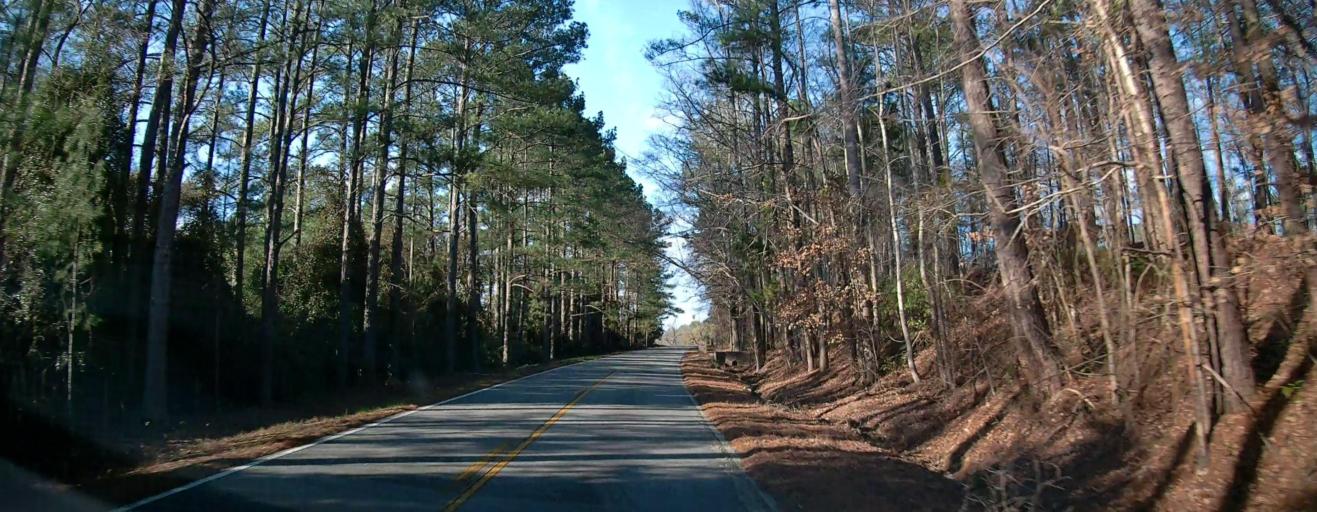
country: US
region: Georgia
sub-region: Harris County
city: Hamilton
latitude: 32.5538
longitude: -84.7796
